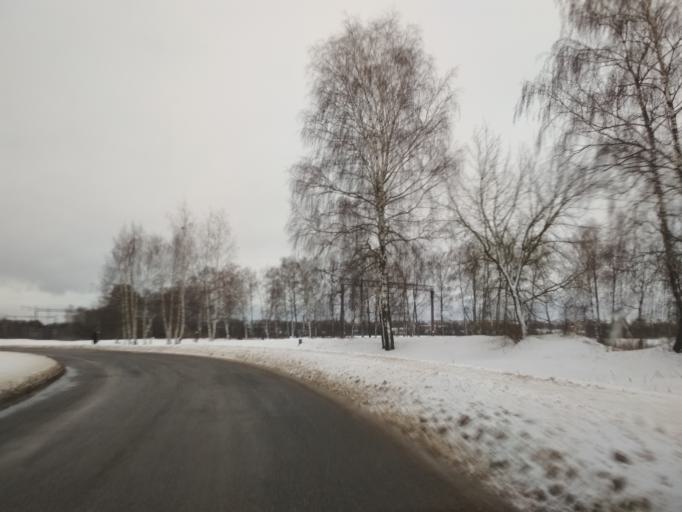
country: BY
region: Minsk
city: Mar''ina Horka
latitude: 53.5288
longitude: 28.1299
